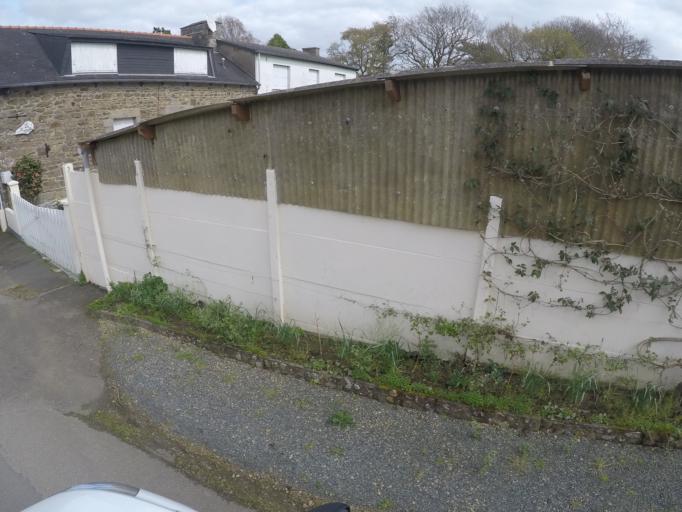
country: FR
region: Brittany
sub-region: Departement des Cotes-d'Armor
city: Plouezec
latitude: 48.7198
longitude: -2.9518
